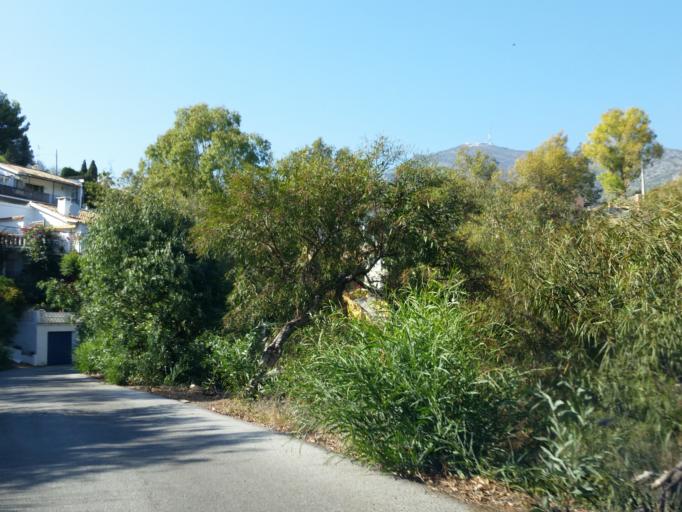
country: ES
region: Andalusia
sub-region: Provincia de Malaga
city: Mijas
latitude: 36.5750
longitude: -4.6067
